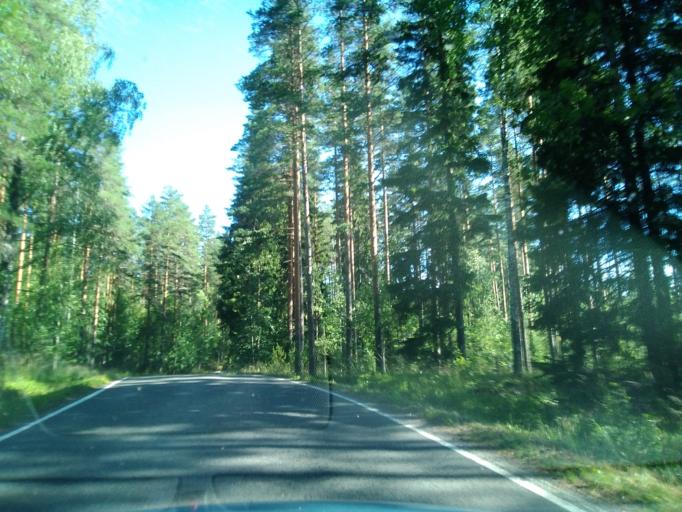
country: FI
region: Uusimaa
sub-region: Helsinki
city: Kaerkoelae
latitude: 60.7831
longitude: 24.0791
